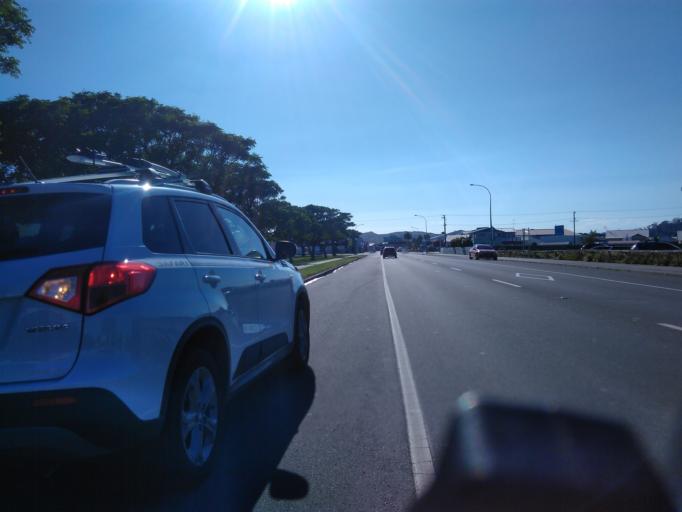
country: NZ
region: Gisborne
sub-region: Gisborne District
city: Gisborne
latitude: -38.6614
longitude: 178.0135
